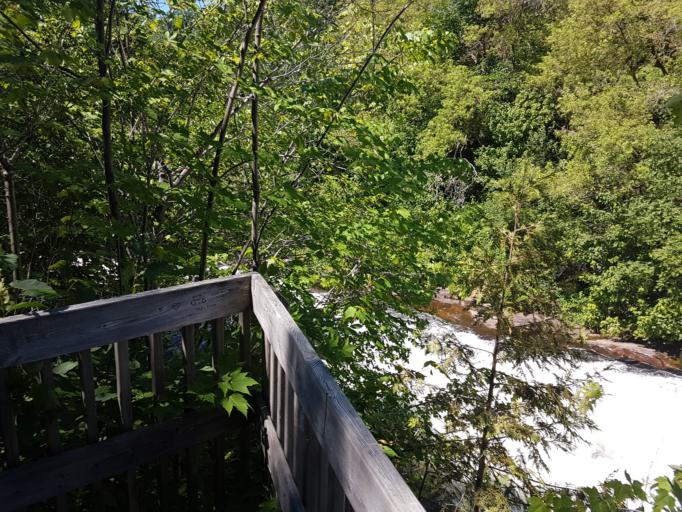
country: CA
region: Quebec
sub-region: Abitibi-Temiscamingue
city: Temiscaming
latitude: 46.7195
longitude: -79.0954
